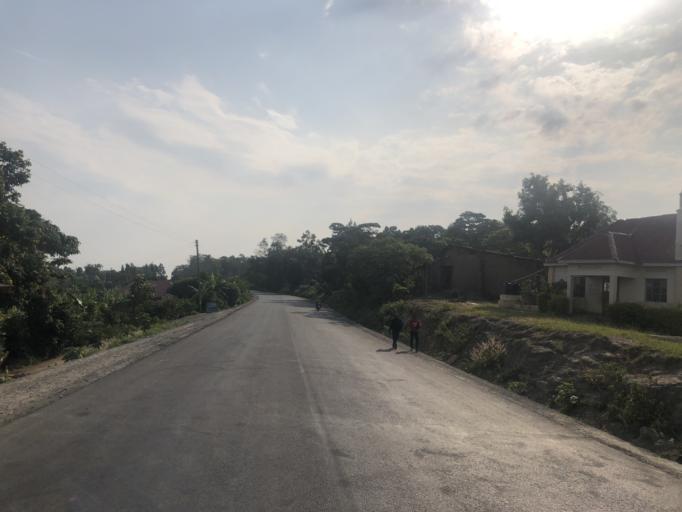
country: UG
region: Western Region
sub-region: Rubirizi District
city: Rubirizi
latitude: -0.2469
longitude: 30.0907
